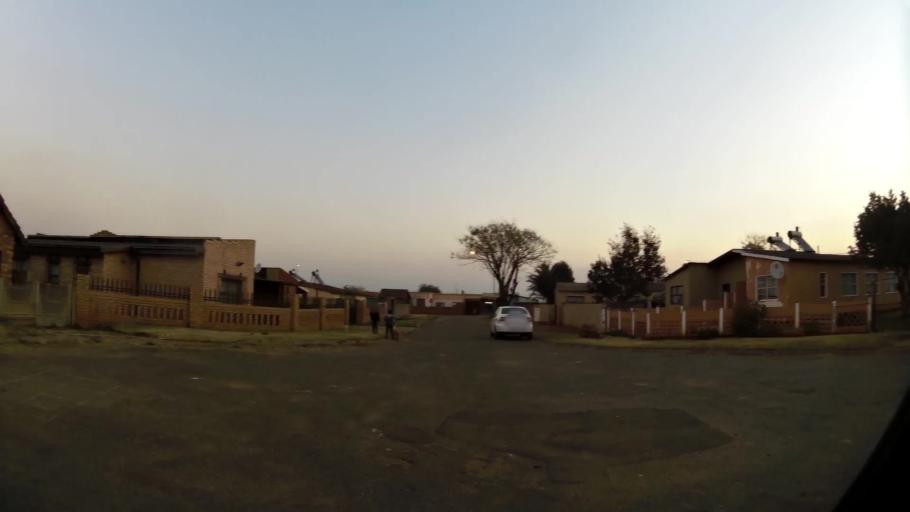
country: ZA
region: Gauteng
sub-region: City of Johannesburg Metropolitan Municipality
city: Soweto
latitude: -26.2908
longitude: 27.8757
